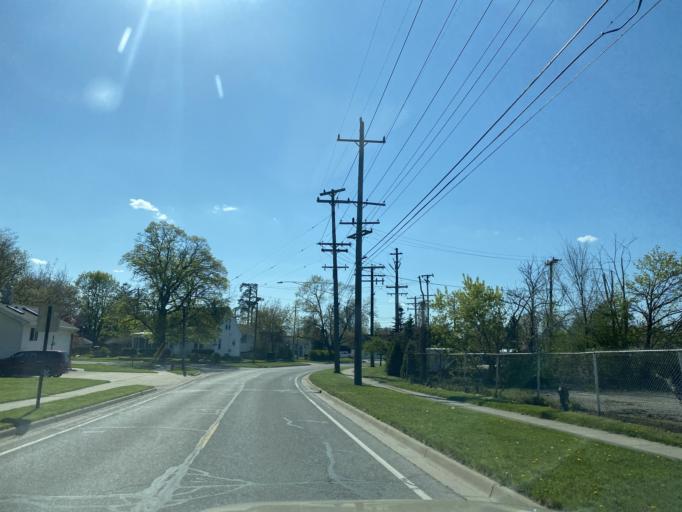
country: US
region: Michigan
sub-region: Livingston County
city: Howell
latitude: 42.6058
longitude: -83.9193
